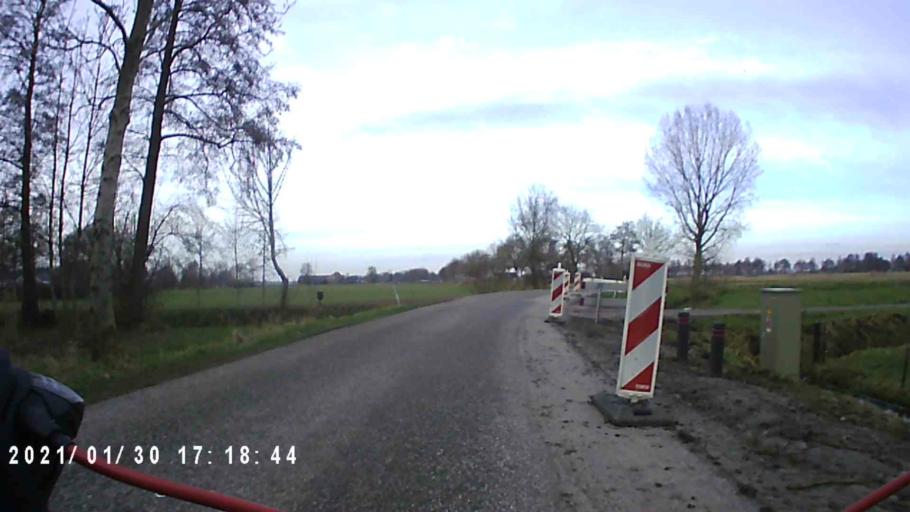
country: NL
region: Groningen
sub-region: Gemeente Leek
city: Leek
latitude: 53.1867
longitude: 6.3569
